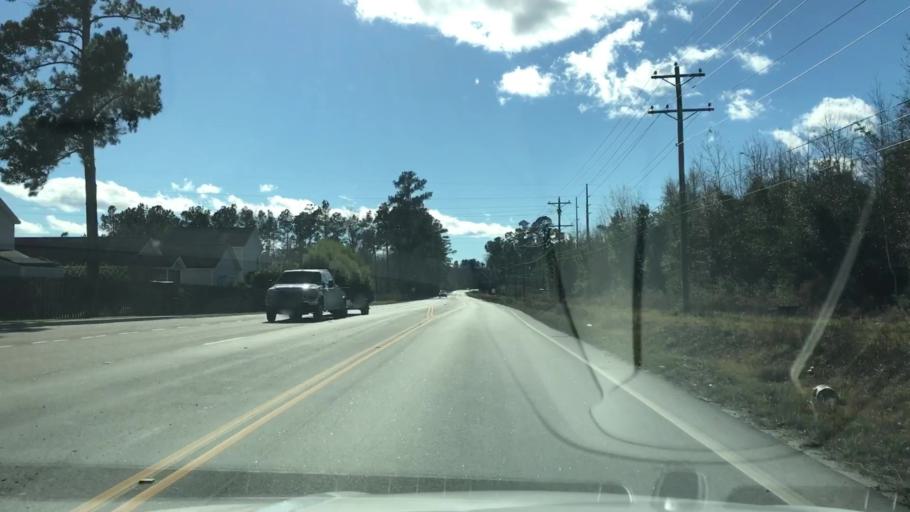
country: US
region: South Carolina
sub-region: Dorchester County
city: Summerville
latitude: 33.0895
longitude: -80.1991
